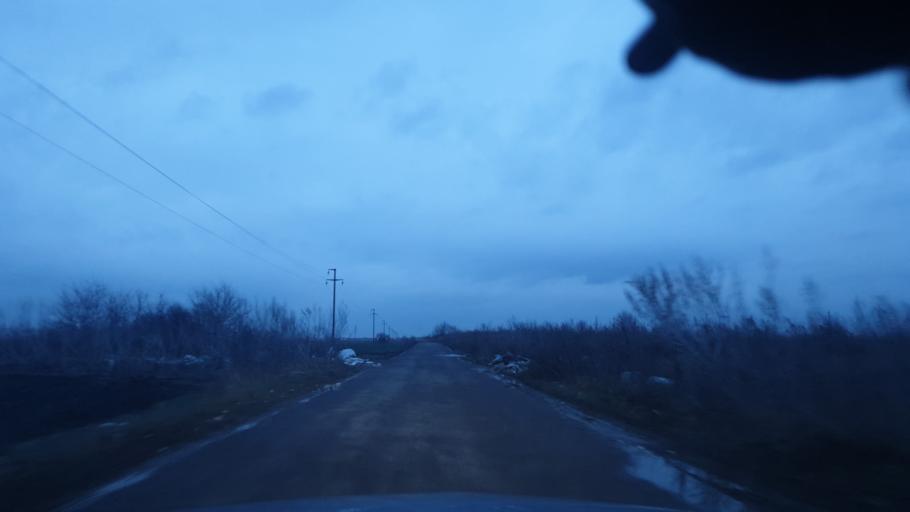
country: RS
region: Autonomna Pokrajina Vojvodina
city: Nova Pazova
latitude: 44.9266
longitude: 20.2162
